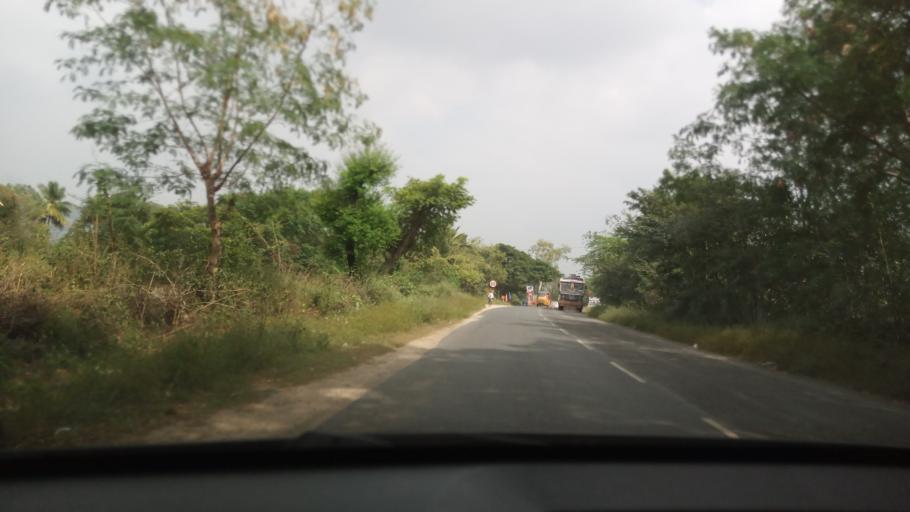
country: IN
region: Andhra Pradesh
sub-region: Chittoor
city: Madanapalle
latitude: 13.6520
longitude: 78.8241
